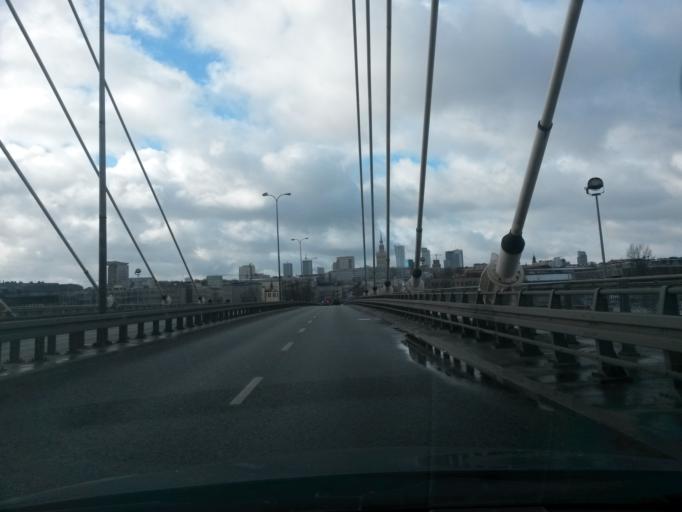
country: PL
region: Masovian Voivodeship
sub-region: Warszawa
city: Praga Polnoc
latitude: 52.2418
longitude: 21.0340
